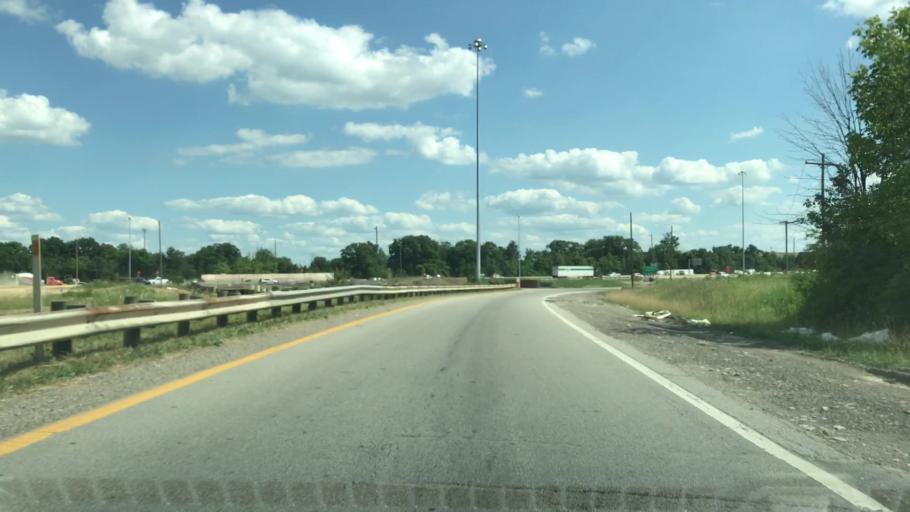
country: US
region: Ohio
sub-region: Franklin County
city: Grove City
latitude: 39.8922
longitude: -83.0420
